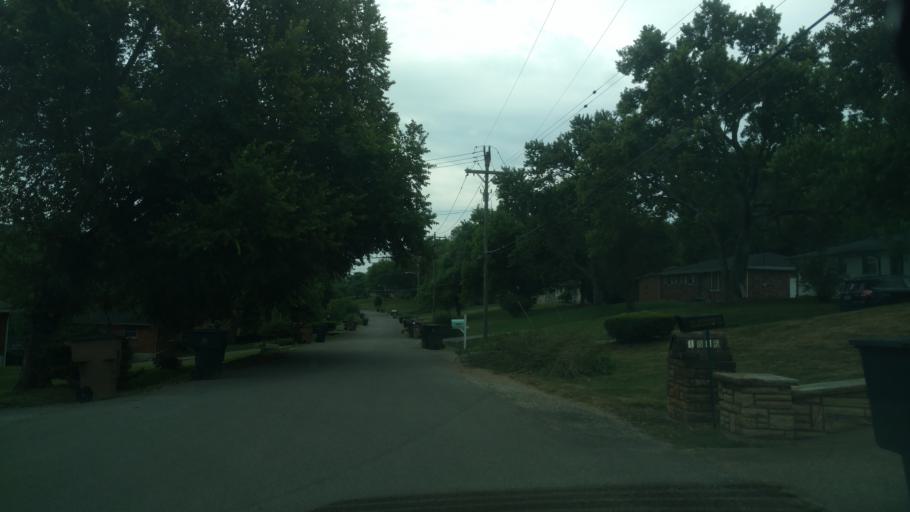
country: US
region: Tennessee
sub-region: Davidson County
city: Nashville
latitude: 36.2005
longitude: -86.7082
